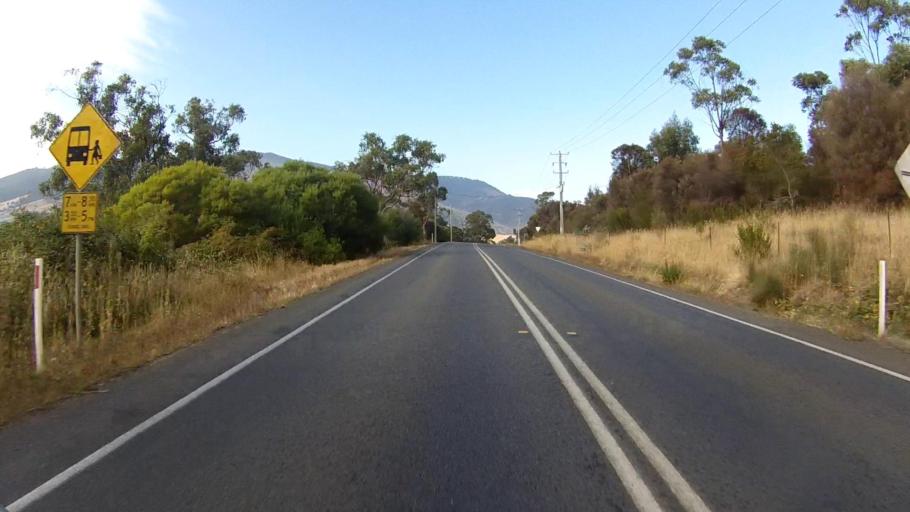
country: AU
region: Tasmania
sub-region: Brighton
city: Bridgewater
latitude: -42.7305
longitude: 147.1777
